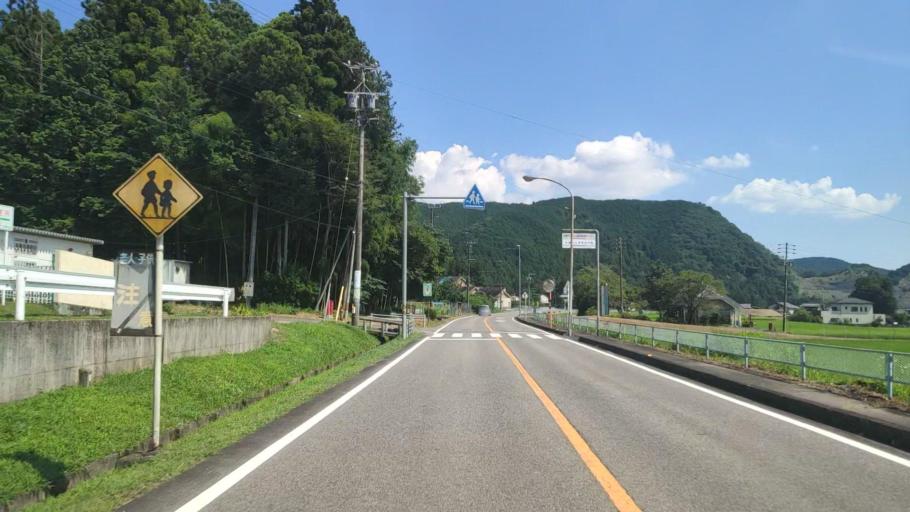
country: JP
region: Gifu
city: Godo
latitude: 35.5371
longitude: 136.6494
